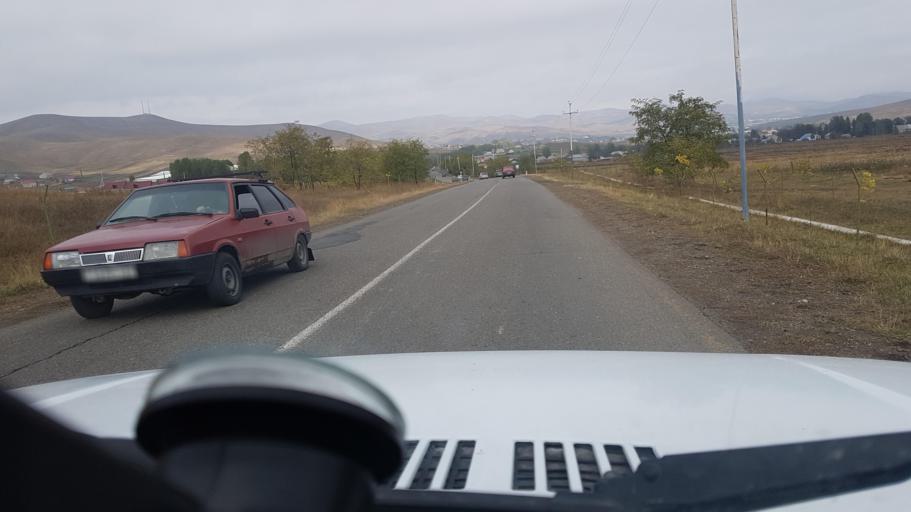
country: AZ
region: Gadabay Rayon
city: Ariqdam
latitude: 40.6256
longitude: 45.8171
